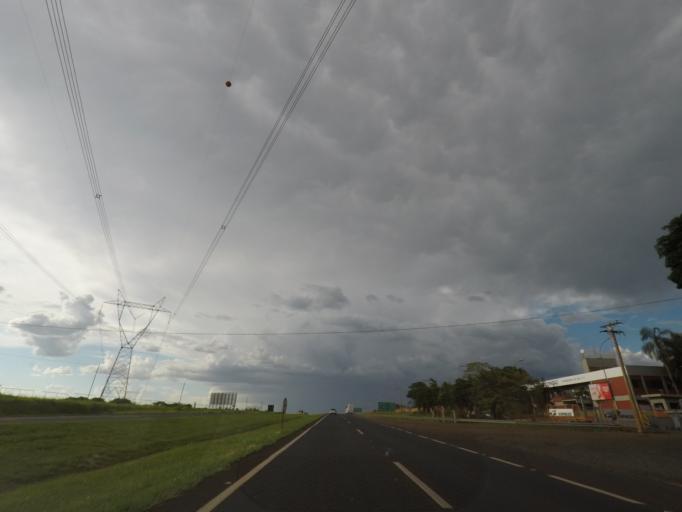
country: BR
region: Sao Paulo
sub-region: Jardinopolis
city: Jardinopolis
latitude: -21.0383
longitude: -47.8313
